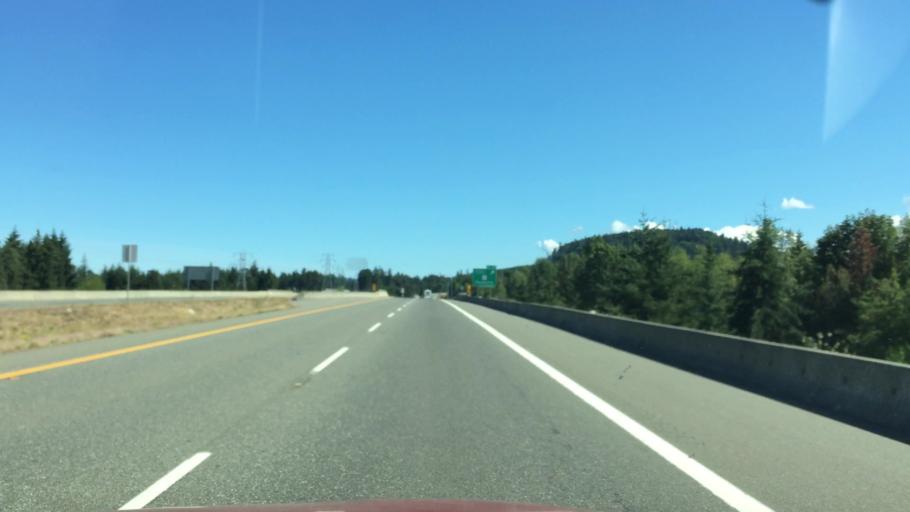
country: CA
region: British Columbia
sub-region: Regional District of Nanaimo
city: Parksville
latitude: 49.3099
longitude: -124.3419
